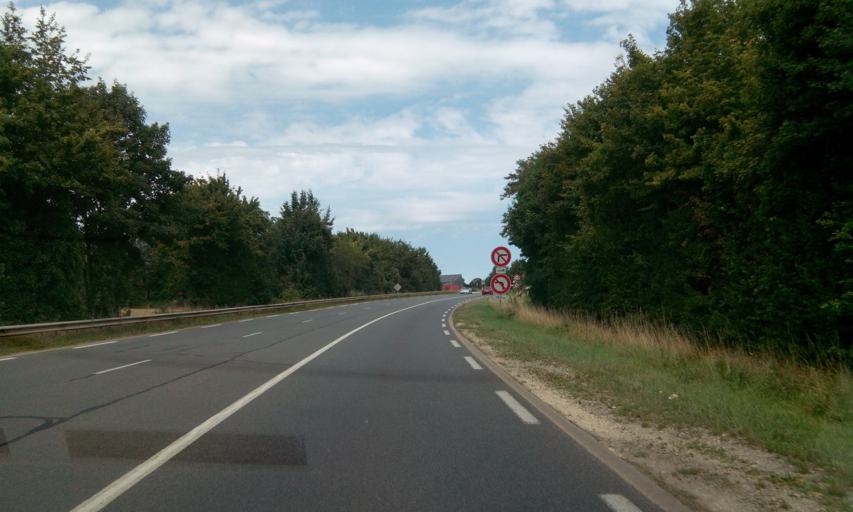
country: FR
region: Poitou-Charentes
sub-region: Departement des Deux-Sevres
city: Melle
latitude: 46.2143
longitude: -0.1572
